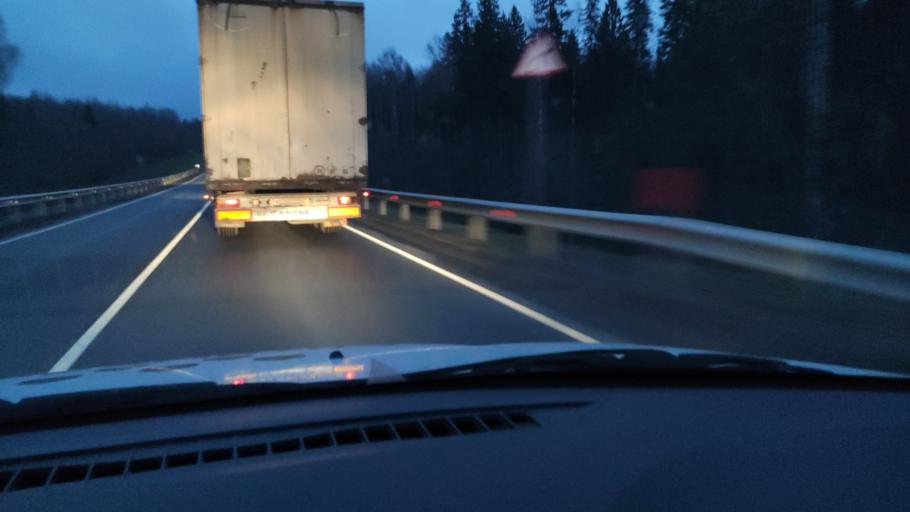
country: RU
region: Kirov
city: Kostino
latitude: 58.8338
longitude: 53.4919
